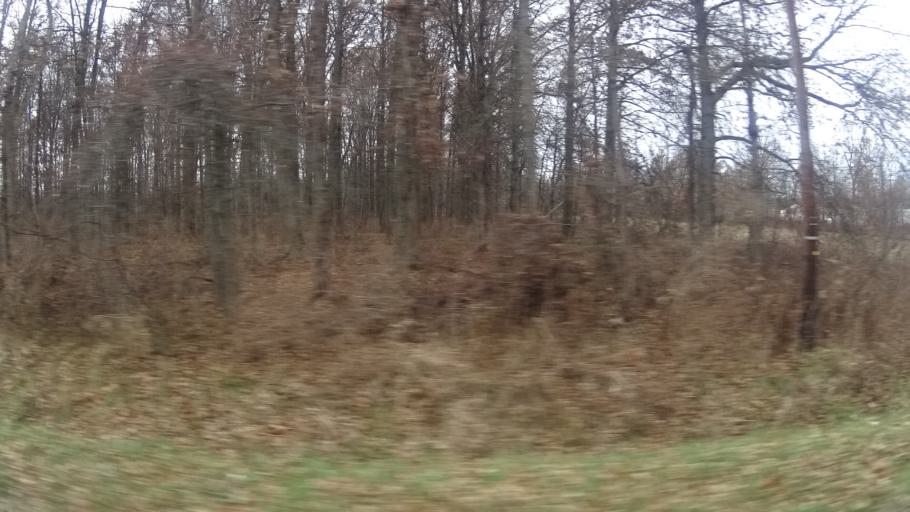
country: US
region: Ohio
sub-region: Cuyahoga County
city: Olmsted Falls
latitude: 41.3319
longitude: -81.9433
